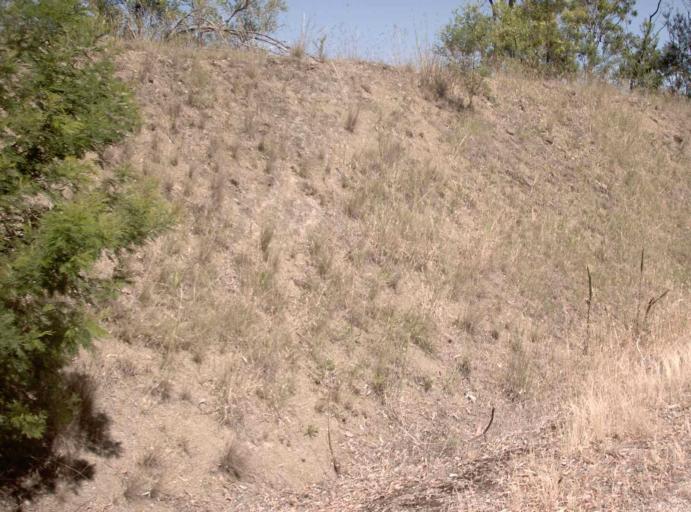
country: AU
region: Victoria
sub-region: East Gippsland
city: Lakes Entrance
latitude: -37.4856
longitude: 148.1870
